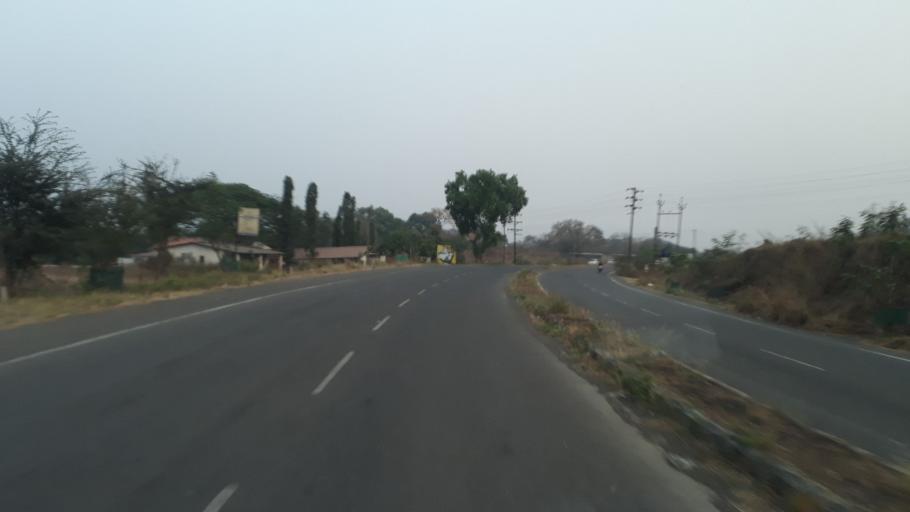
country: IN
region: Maharashtra
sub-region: Raigarh
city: Neral
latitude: 19.0141
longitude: 73.3245
